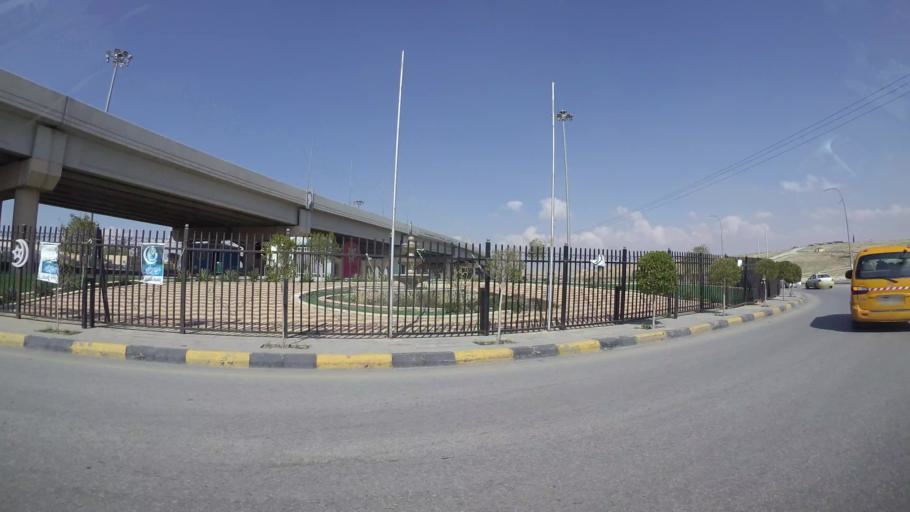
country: JO
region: Zarqa
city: Zarqa
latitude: 32.0806
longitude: 36.1069
